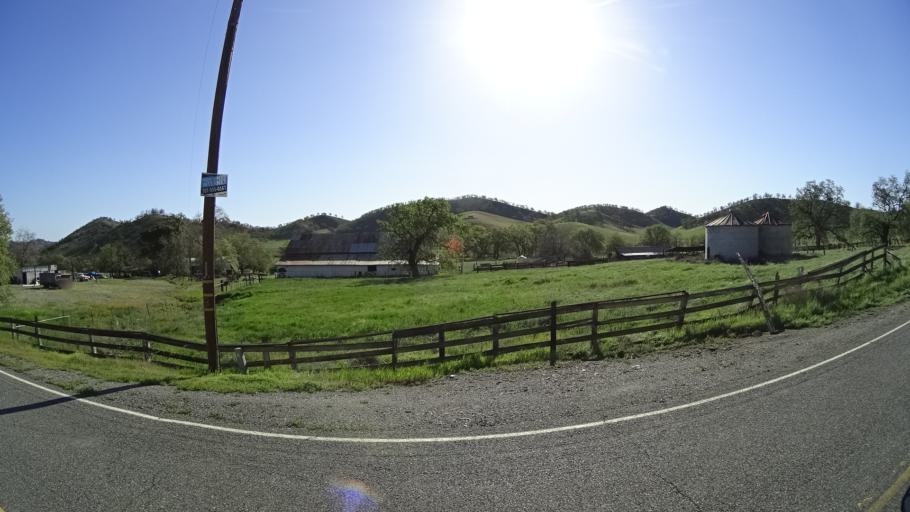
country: US
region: California
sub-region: Tehama County
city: Rancho Tehama Reserve
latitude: 39.7732
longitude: -122.5222
